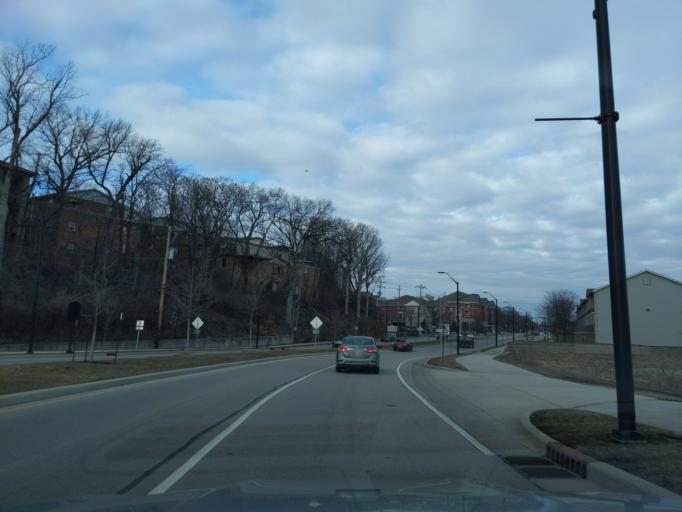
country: US
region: Indiana
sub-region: Tippecanoe County
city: West Lafayette
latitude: 40.4188
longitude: -86.9060
